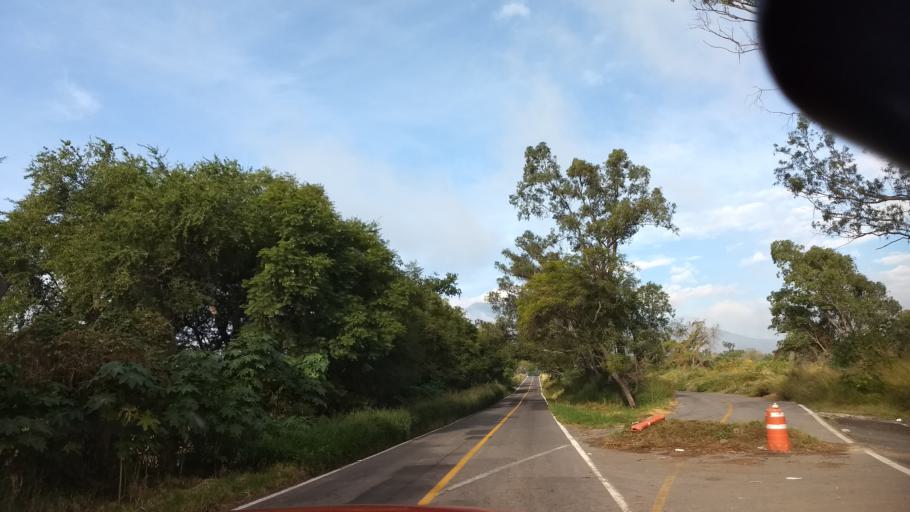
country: MX
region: Jalisco
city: Tuxpan
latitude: 19.5229
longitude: -103.4429
